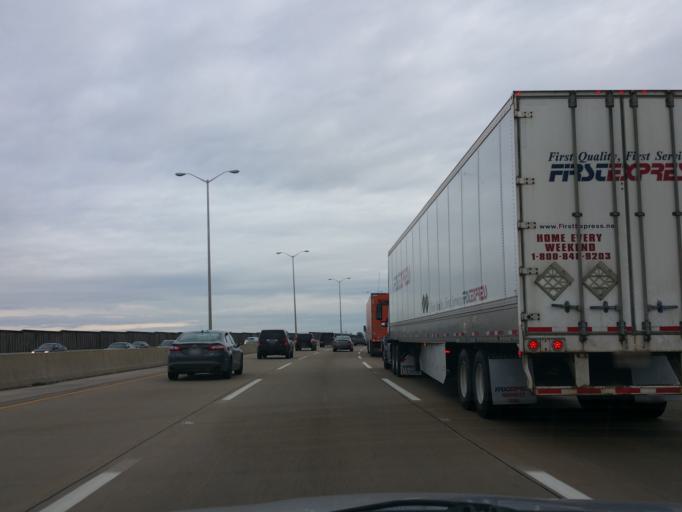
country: US
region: Illinois
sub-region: Cook County
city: Chicago Ridge
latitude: 41.7018
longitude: -87.7873
